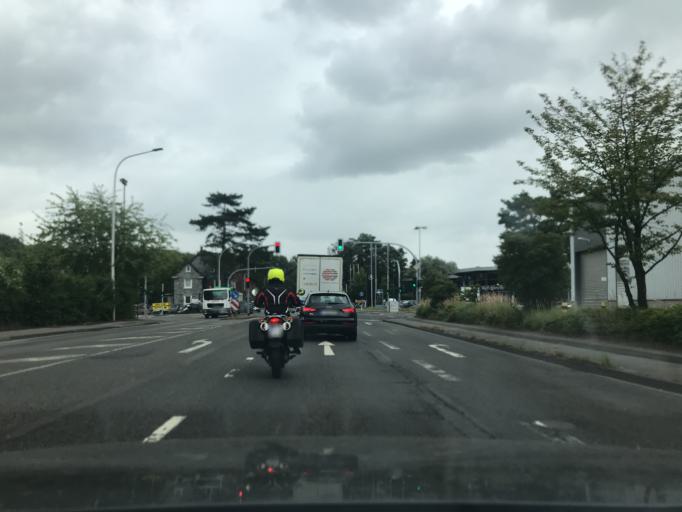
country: DE
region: North Rhine-Westphalia
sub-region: Regierungsbezirk Dusseldorf
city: Hilden
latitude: 51.1722
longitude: 6.9069
